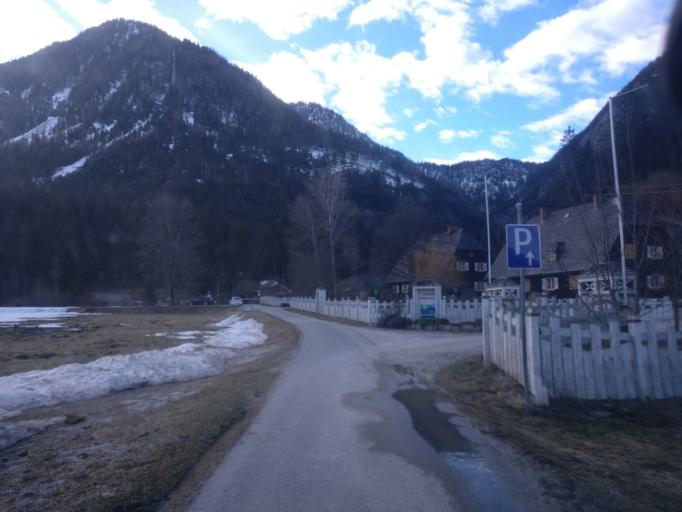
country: AT
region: Styria
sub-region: Politischer Bezirk Liezen
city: Sankt Martin am Grimming
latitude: 47.4899
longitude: 13.9601
